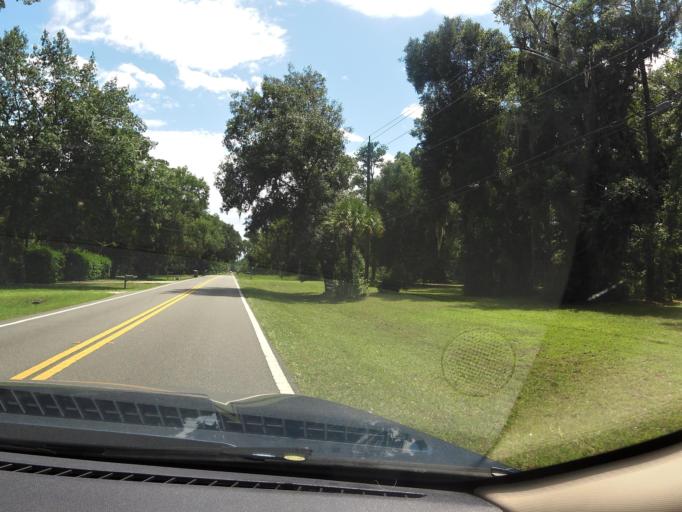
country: US
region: Florida
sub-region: Nassau County
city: Fernandina Beach
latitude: 30.6583
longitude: -81.5263
